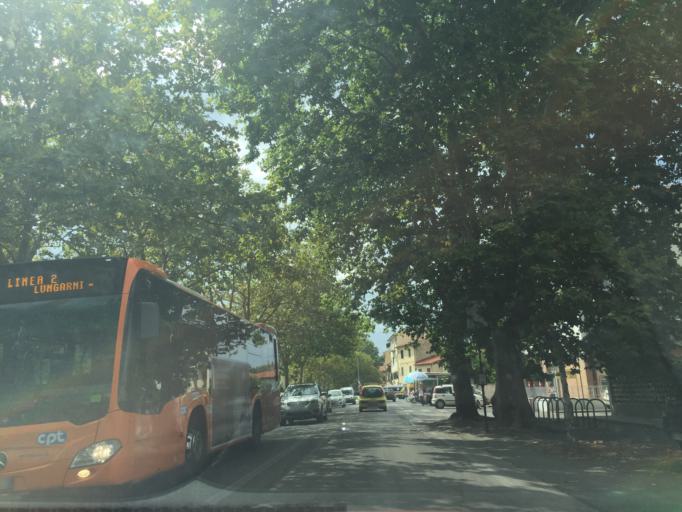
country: IT
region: Tuscany
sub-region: Province of Pisa
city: Pisa
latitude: 43.7254
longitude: 10.4052
